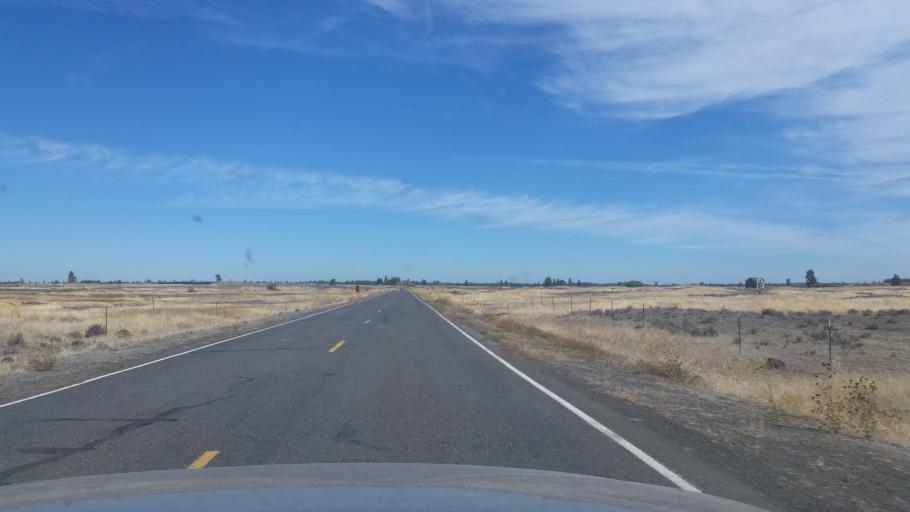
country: US
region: Washington
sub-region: Spokane County
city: Medical Lake
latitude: 47.3884
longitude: -117.8412
